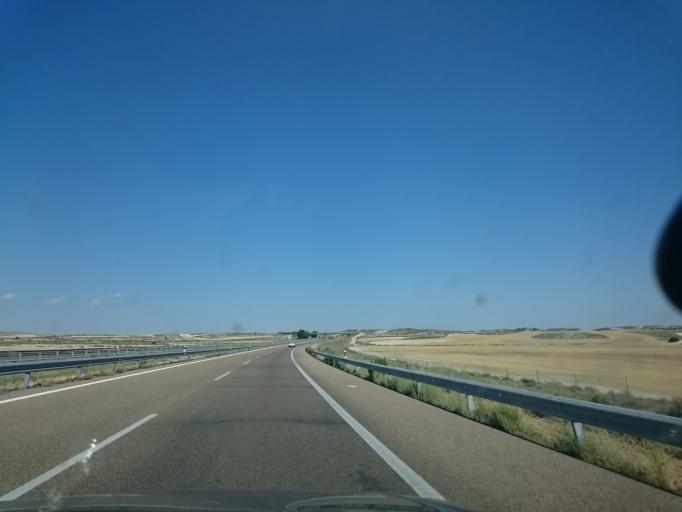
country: ES
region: Aragon
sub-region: Provincia de Huesca
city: Castejon de Monegros
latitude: 41.5190
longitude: -0.2728
